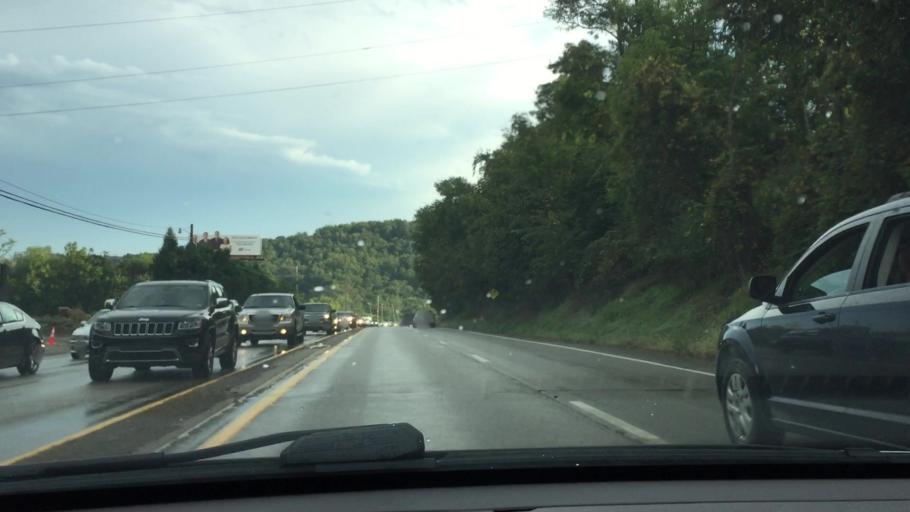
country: US
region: Pennsylvania
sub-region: Washington County
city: Canonsburg
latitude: 40.2355
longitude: -80.1790
